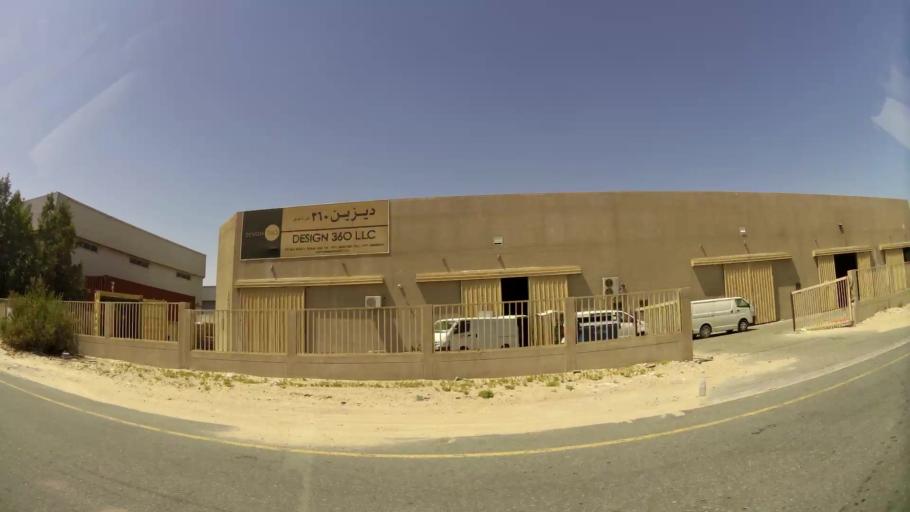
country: AE
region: Dubai
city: Dubai
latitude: 24.9871
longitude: 55.2105
